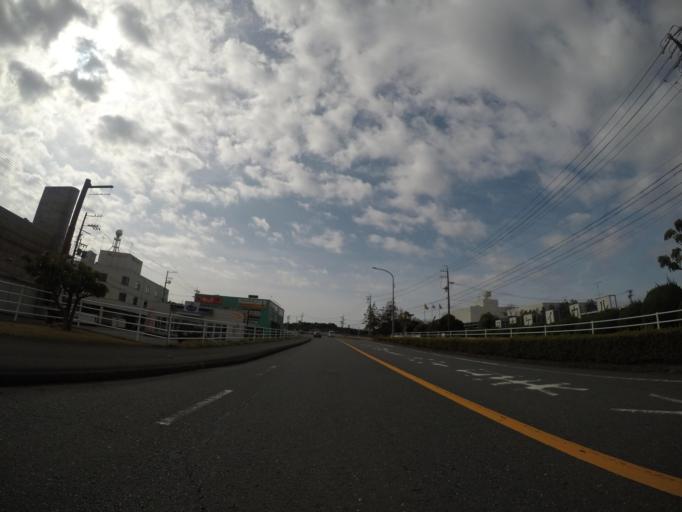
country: JP
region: Shizuoka
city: Hamakita
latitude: 34.8116
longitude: 137.6851
